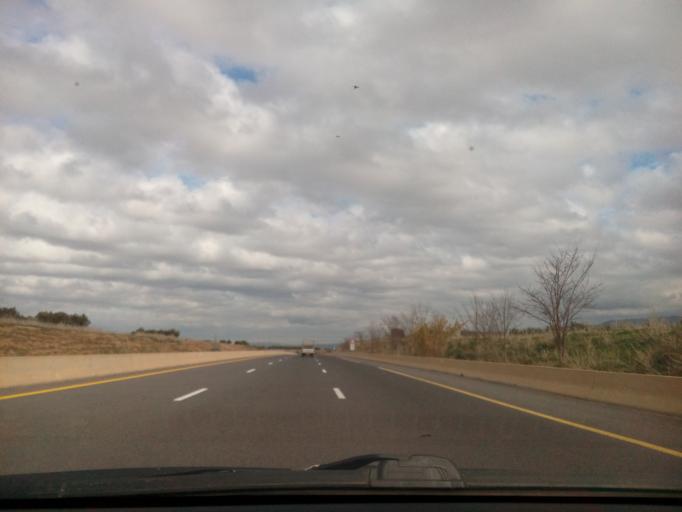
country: DZ
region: Tlemcen
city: Chetouane
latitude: 34.9726
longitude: -1.2606
